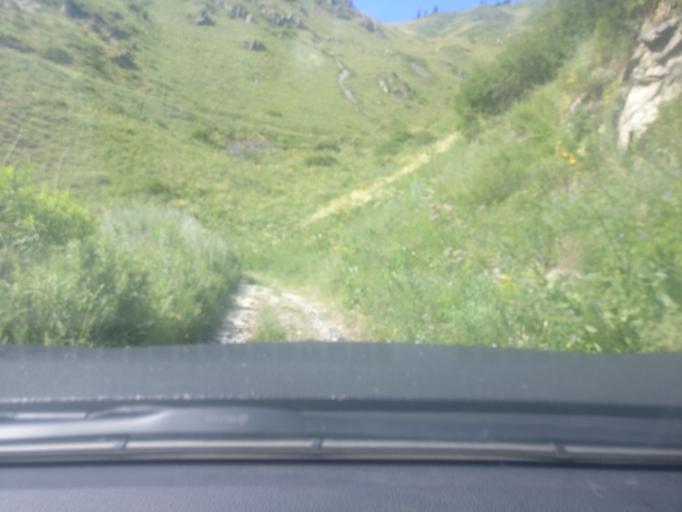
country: KZ
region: Almaty Qalasy
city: Almaty
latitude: 43.0981
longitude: 76.9555
